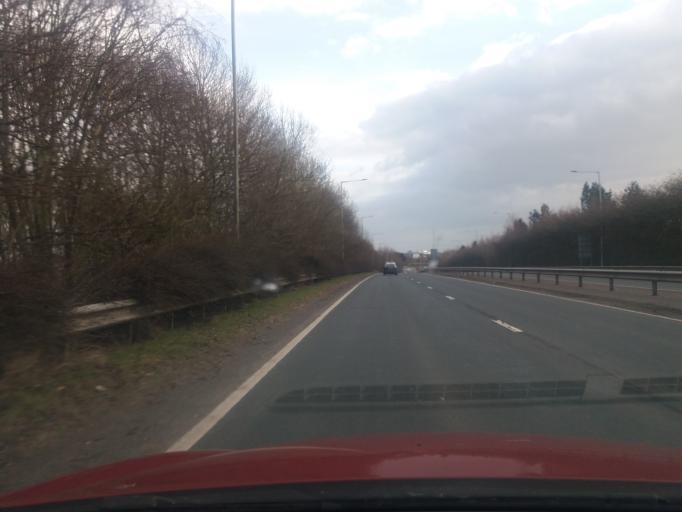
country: GB
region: England
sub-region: Lancashire
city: Clayton-le-Woods
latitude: 53.7267
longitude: -2.6735
